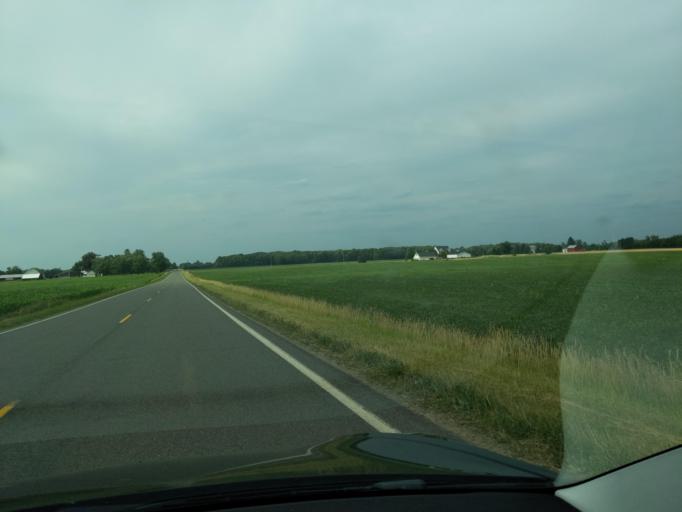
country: US
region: Michigan
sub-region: Clinton County
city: DeWitt
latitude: 42.9098
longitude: -84.6021
